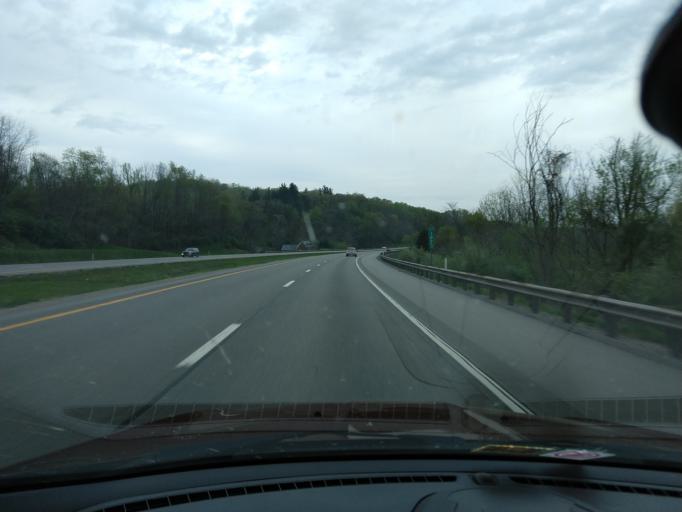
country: US
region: West Virginia
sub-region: Lewis County
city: Weston
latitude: 39.0699
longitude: -80.4049
